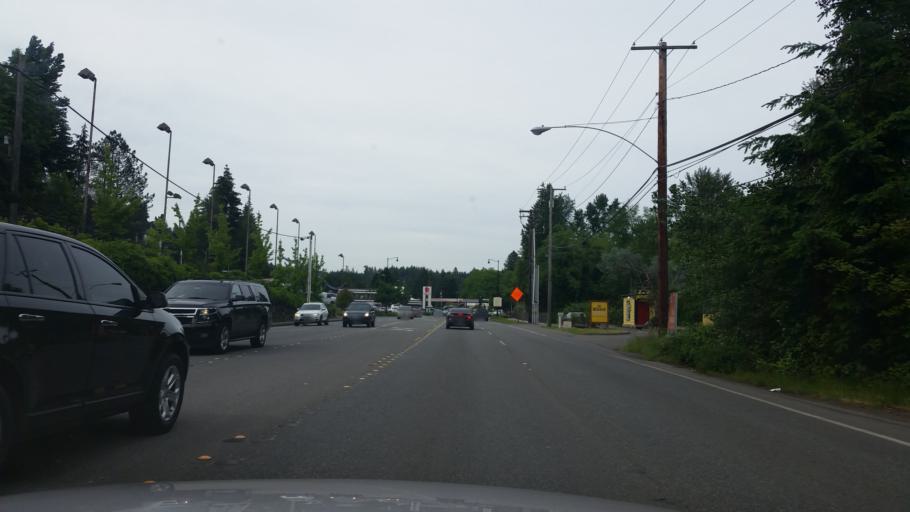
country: US
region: Washington
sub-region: King County
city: Bothell
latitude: 47.7561
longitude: -122.2122
